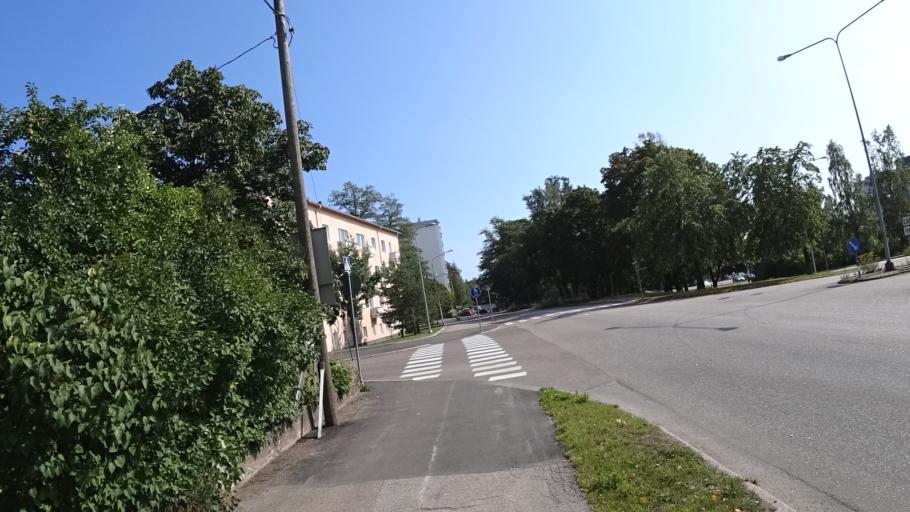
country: FI
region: Kymenlaakso
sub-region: Kotka-Hamina
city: Kotka
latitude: 60.4582
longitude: 26.9295
